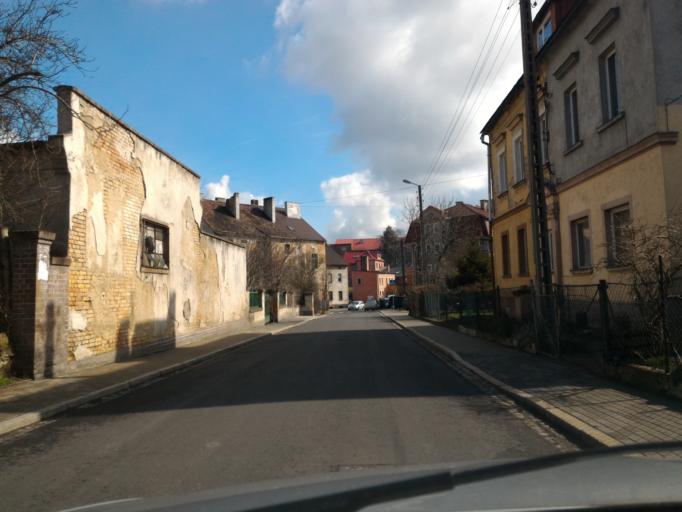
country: PL
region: Silesian Voivodeship
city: Zawidow
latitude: 51.0268
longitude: 15.0604
